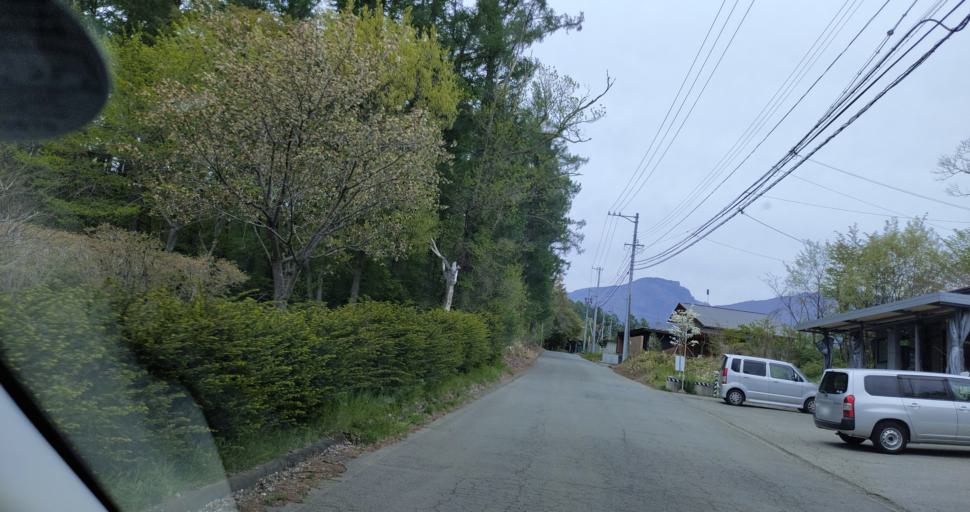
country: JP
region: Nagano
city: Komoro
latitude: 36.3361
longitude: 138.4673
